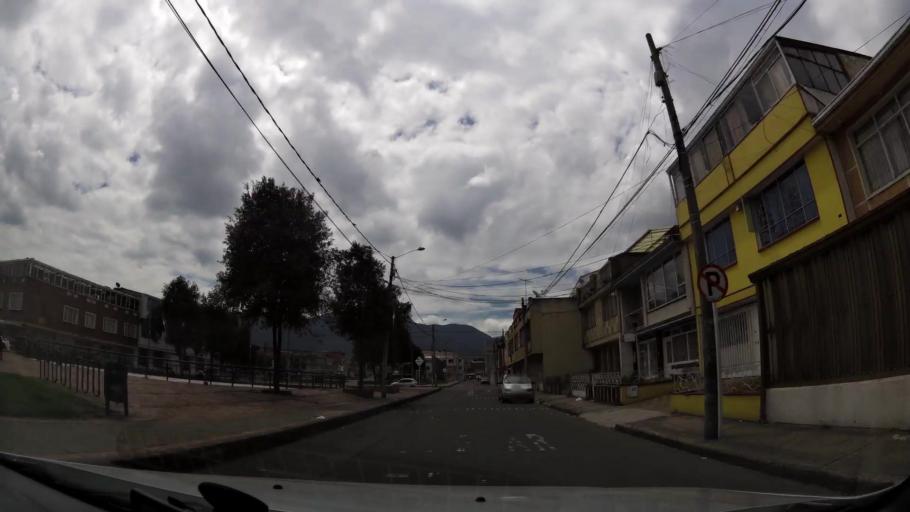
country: CO
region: Bogota D.C.
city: Bogota
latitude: 4.5981
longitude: -74.0993
